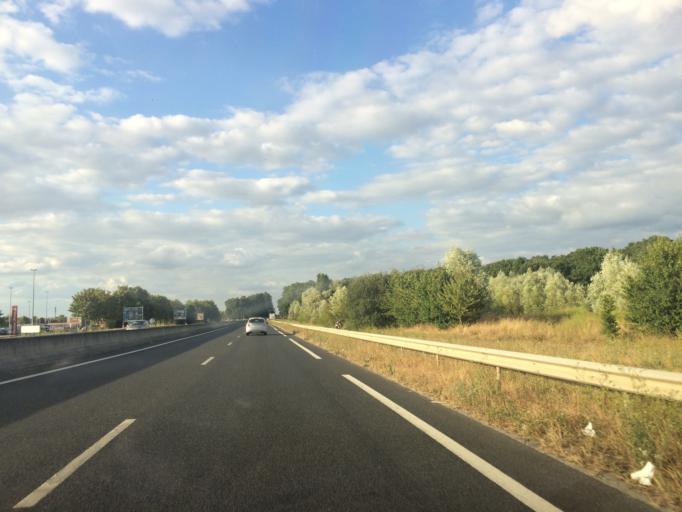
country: FR
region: Ile-de-France
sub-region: Departement de l'Essonne
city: Marolles-en-Hurepoix
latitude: 48.5831
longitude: 2.3053
